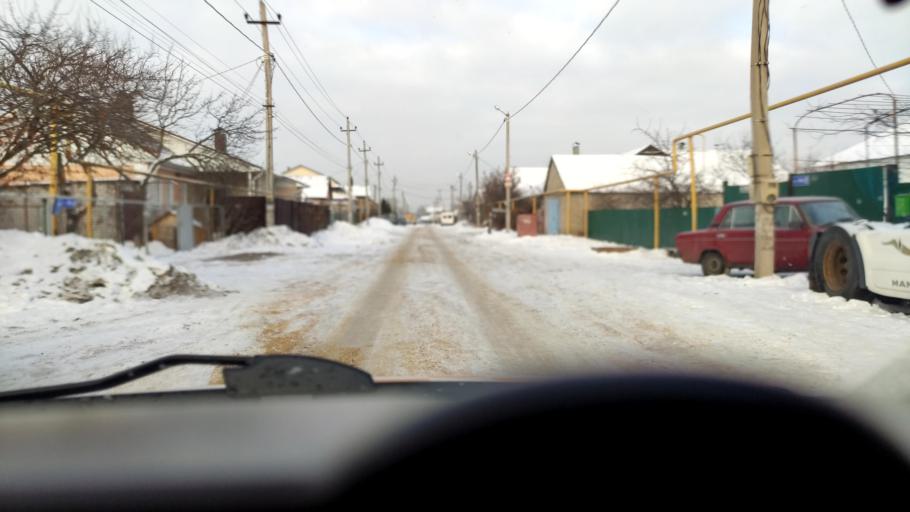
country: RU
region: Voronezj
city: Podgornoye
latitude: 51.7271
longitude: 39.1548
